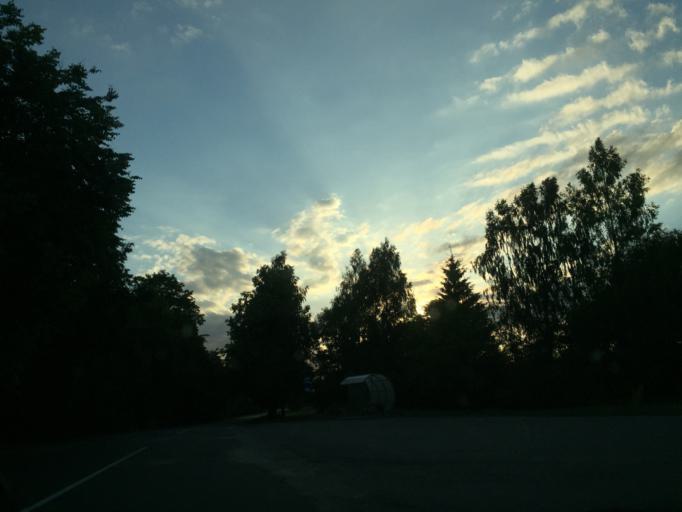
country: LV
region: Sigulda
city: Sigulda
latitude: 57.1404
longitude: 24.8676
